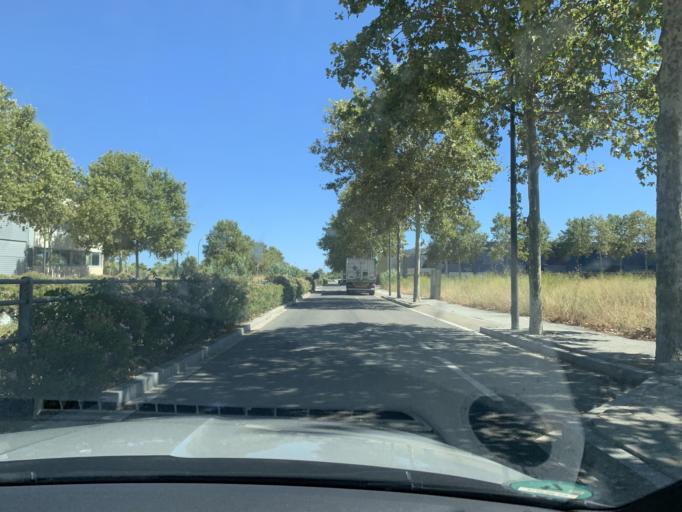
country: ES
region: Catalonia
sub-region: Provincia de Tarragona
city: Reus
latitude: 41.1458
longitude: 1.1273
